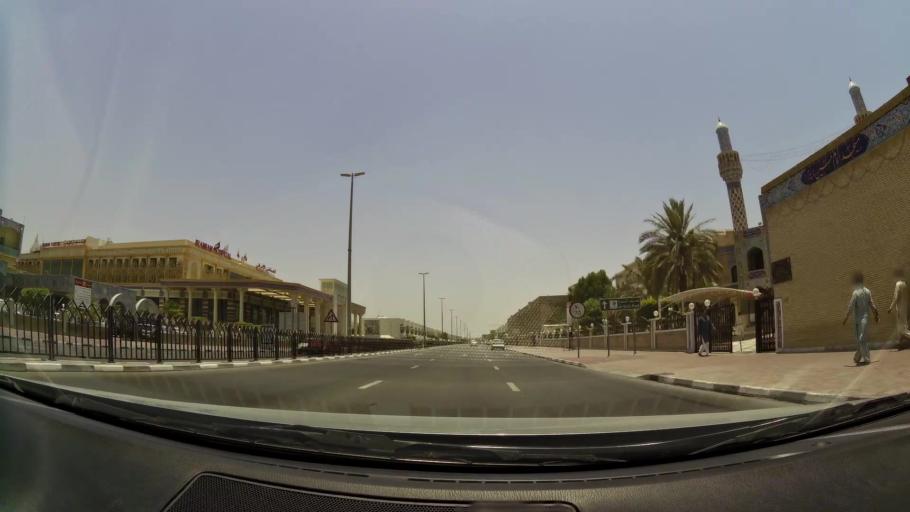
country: AE
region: Ash Shariqah
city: Sharjah
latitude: 25.2308
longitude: 55.2684
